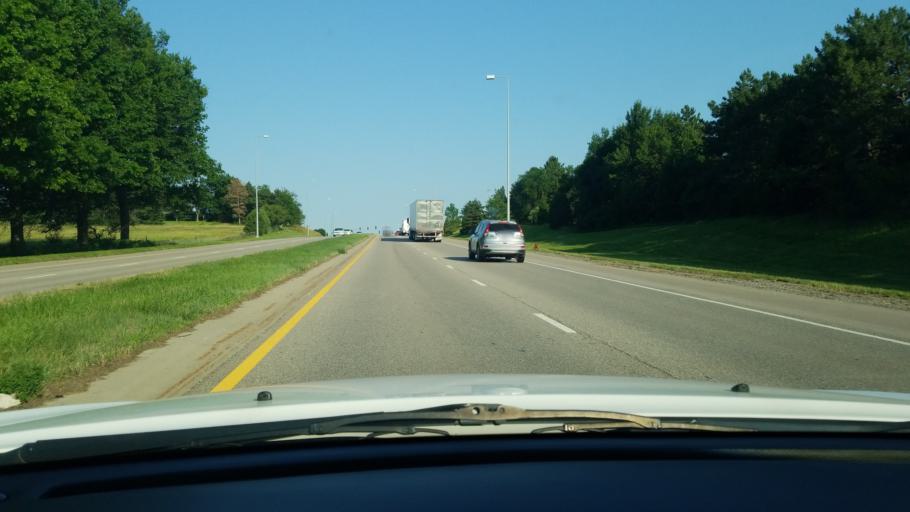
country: US
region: Nebraska
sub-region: Lancaster County
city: Lincoln
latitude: 40.7480
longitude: -96.6288
